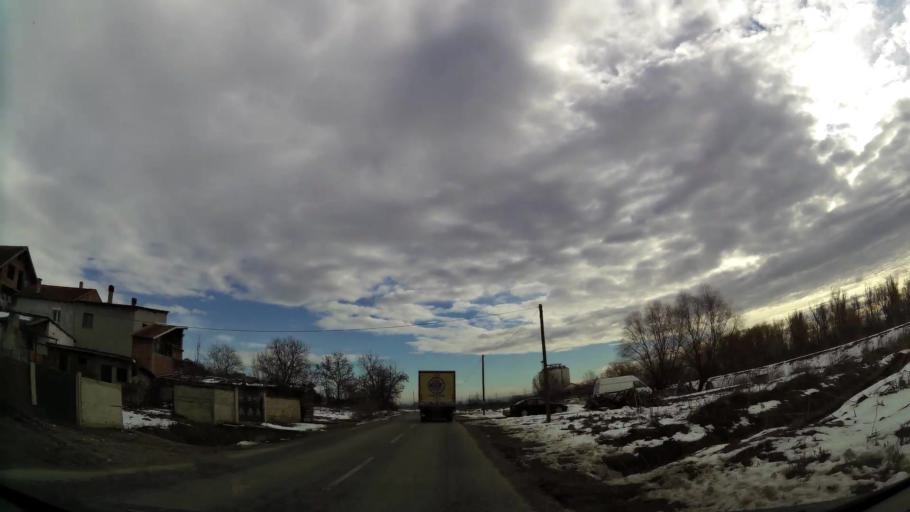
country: RS
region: Central Serbia
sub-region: Belgrade
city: Surcin
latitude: 44.7931
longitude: 20.3040
